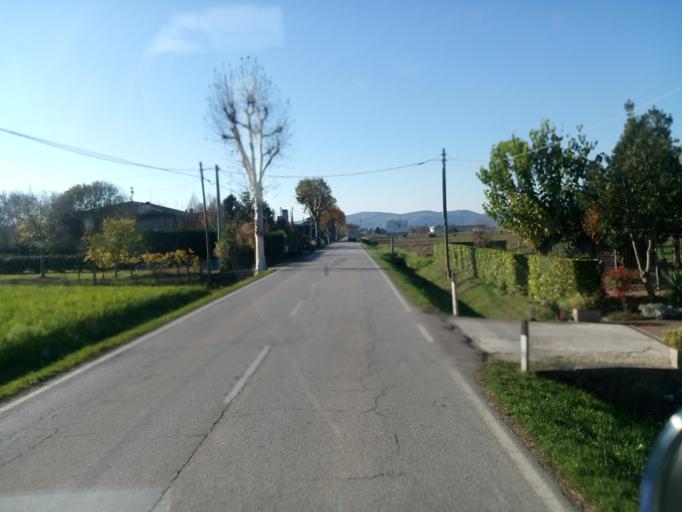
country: IT
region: Veneto
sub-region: Provincia di Vicenza
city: Ponte di Barbarano
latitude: 45.3825
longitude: 11.5890
